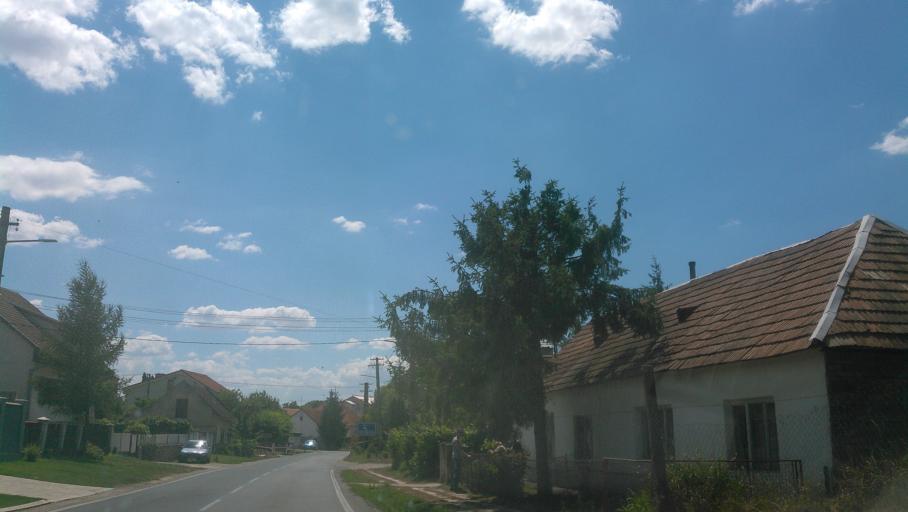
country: SK
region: Trnavsky
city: Leopoldov
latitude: 48.5122
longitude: 17.7243
